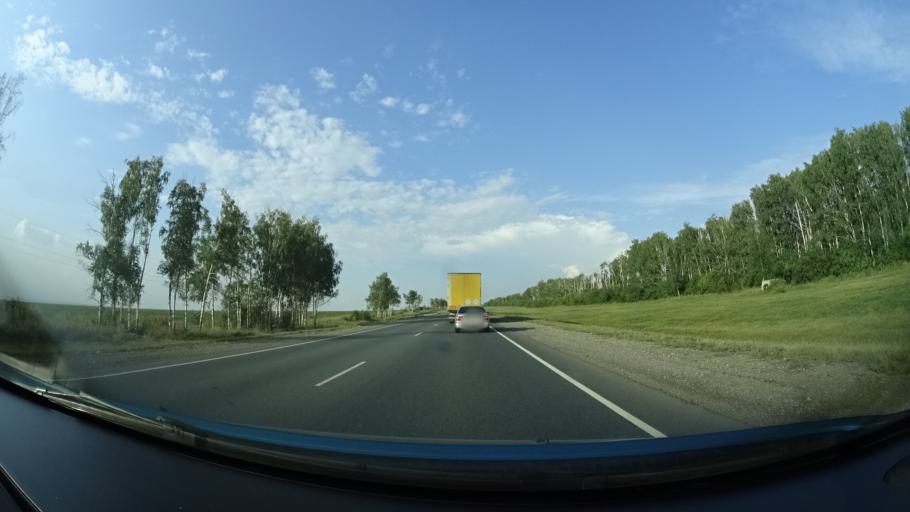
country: RU
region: Samara
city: Krasnyy Yar
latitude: 53.6591
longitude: 50.7523
